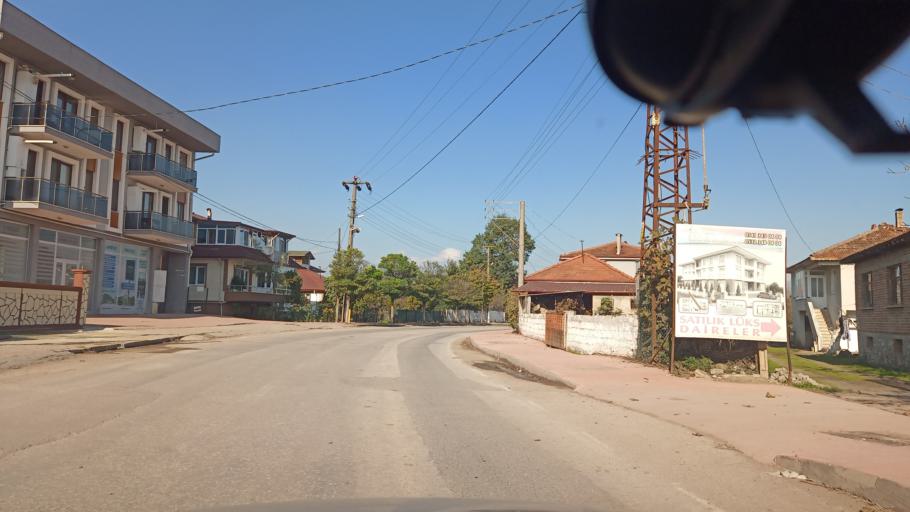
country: TR
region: Sakarya
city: Sogutlu
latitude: 40.9092
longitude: 30.4737
